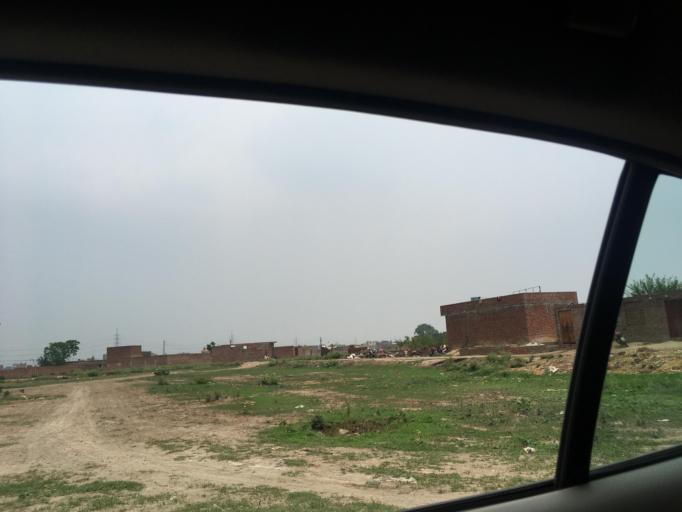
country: PK
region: Punjab
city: Lahore
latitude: 31.6195
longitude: 74.3537
